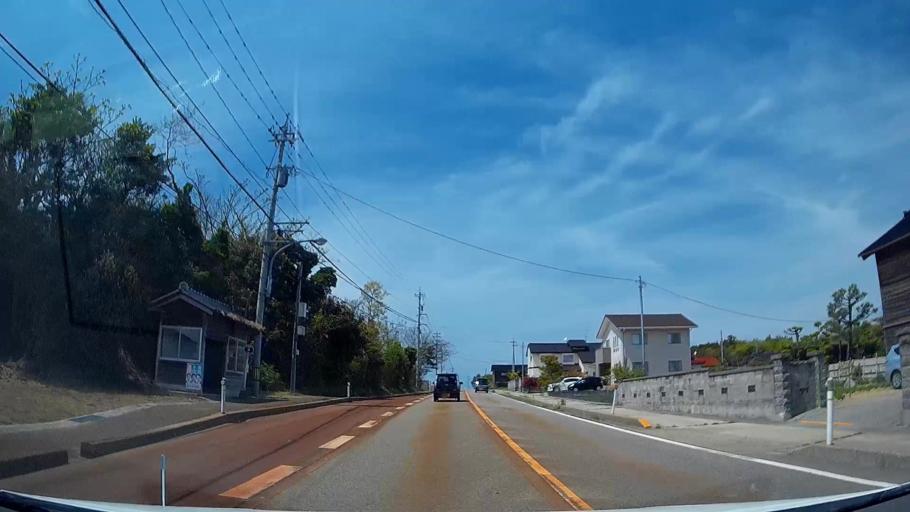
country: JP
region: Ishikawa
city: Hakui
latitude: 36.9268
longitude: 136.7594
